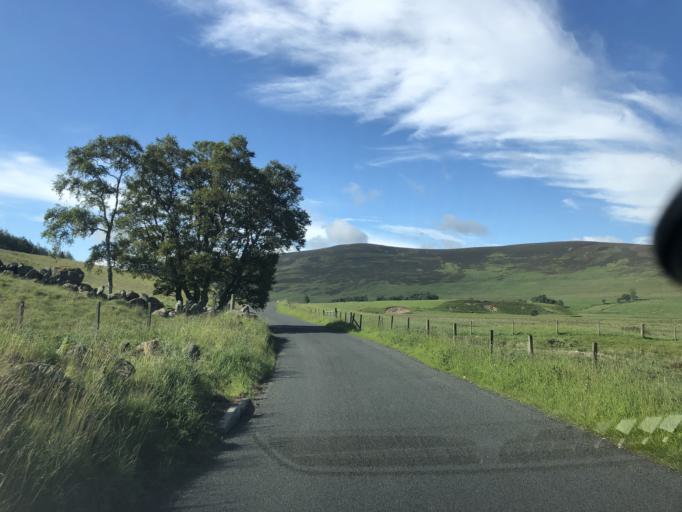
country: GB
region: Scotland
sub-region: Angus
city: Kirriemuir
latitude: 56.8047
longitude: -3.0364
